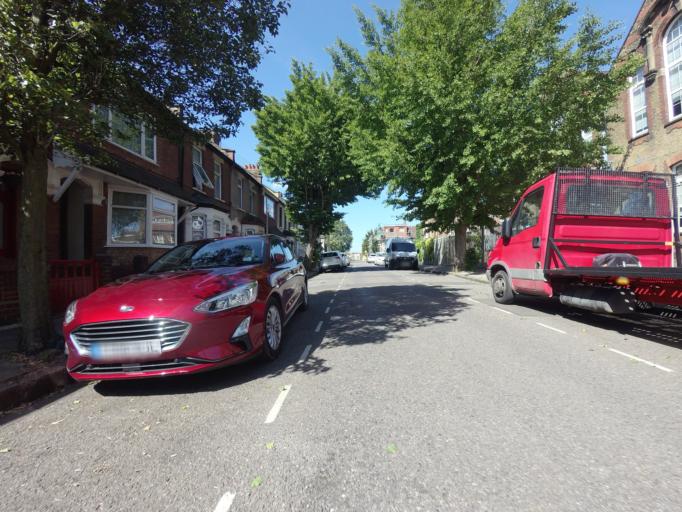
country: GB
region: England
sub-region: Greater London
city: Poplar
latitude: 51.5220
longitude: 0.0084
